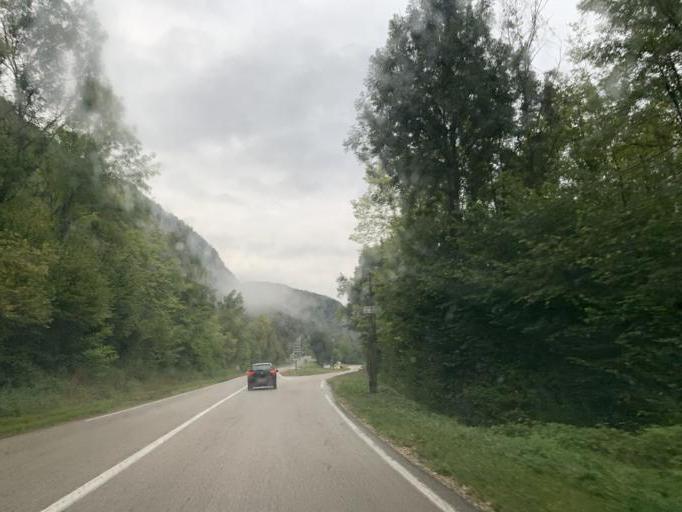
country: FR
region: Rhone-Alpes
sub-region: Departement de l'Isere
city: Les Avenieres
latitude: 45.6744
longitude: 5.6082
